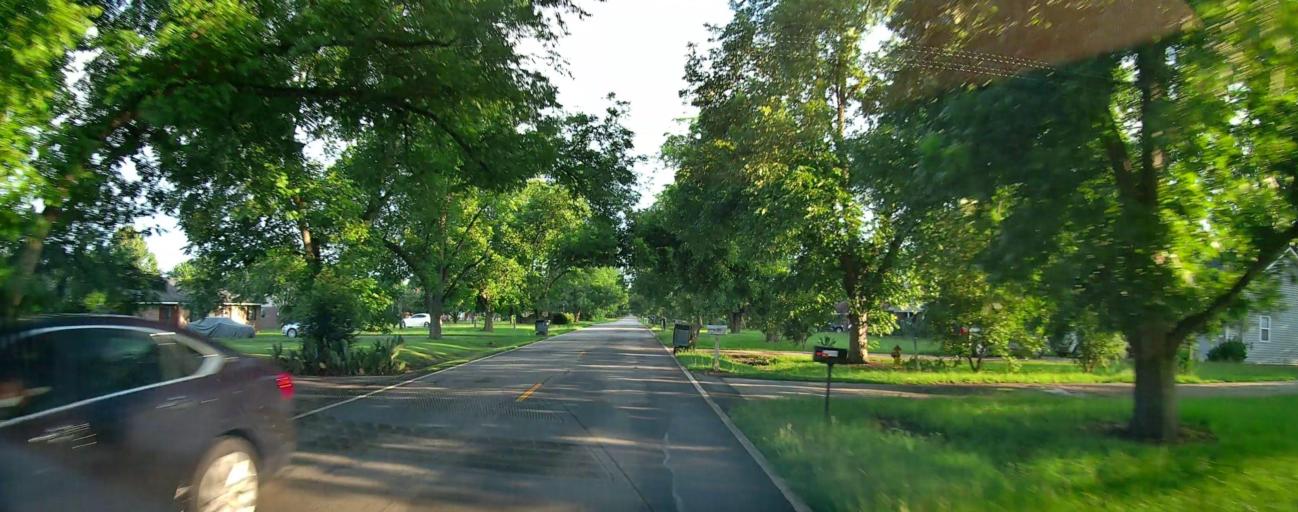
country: US
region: Georgia
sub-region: Peach County
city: Fort Valley
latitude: 32.5849
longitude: -83.8738
